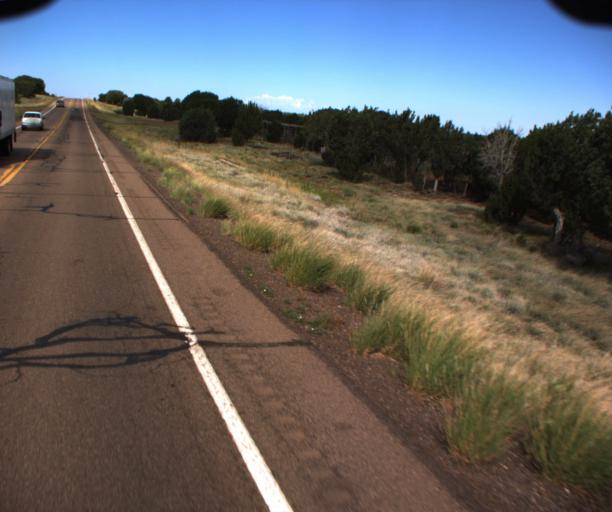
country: US
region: Arizona
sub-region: Navajo County
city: White Mountain Lake
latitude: 34.2720
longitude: -109.9170
